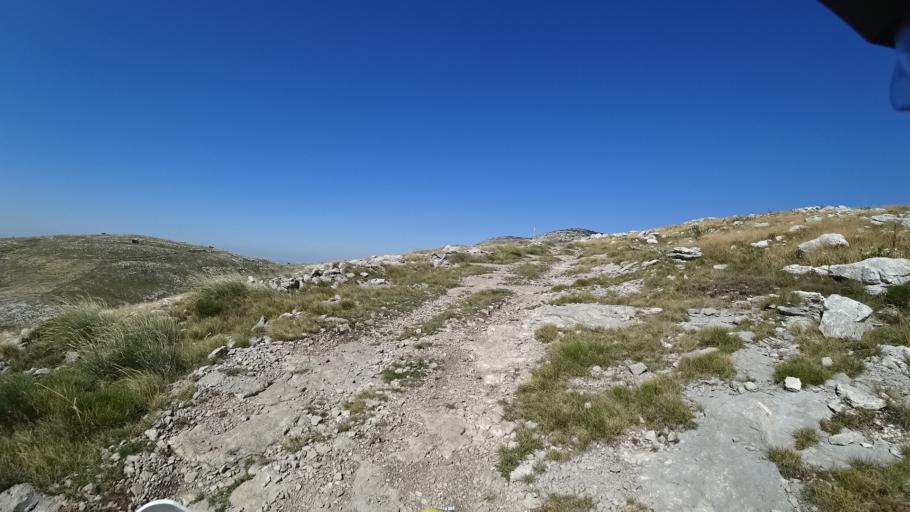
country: HR
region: Splitsko-Dalmatinska
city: Hrvace
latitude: 43.9249
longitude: 16.6070
